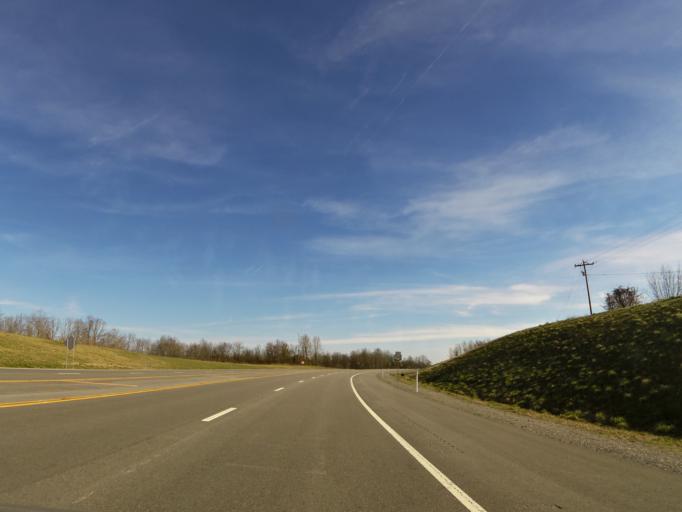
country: US
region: Tennessee
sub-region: Cannon County
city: Woodbury
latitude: 35.7980
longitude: -85.9973
